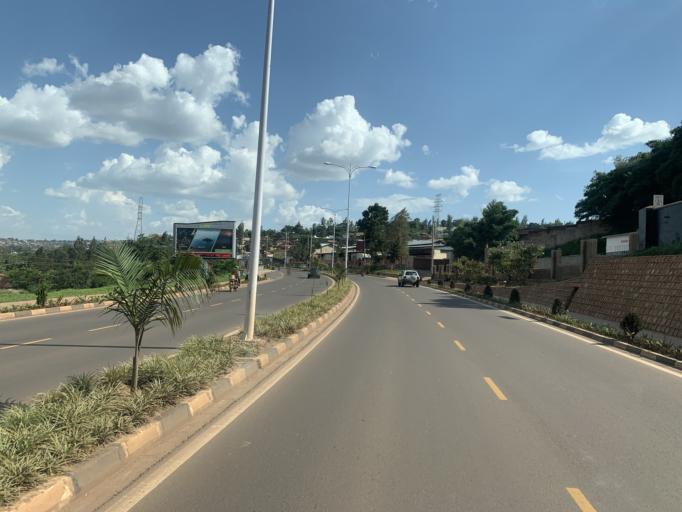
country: RW
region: Kigali
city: Kigali
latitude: -1.9617
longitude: 30.0773
